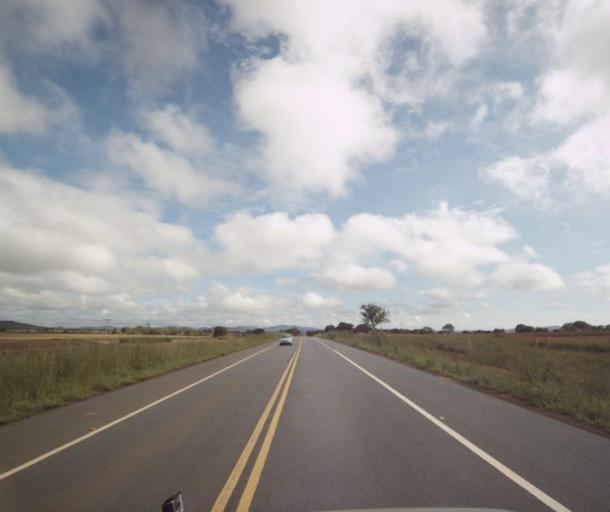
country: BR
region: Goias
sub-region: Barro Alto
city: Barro Alto
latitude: -15.2524
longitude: -48.6882
